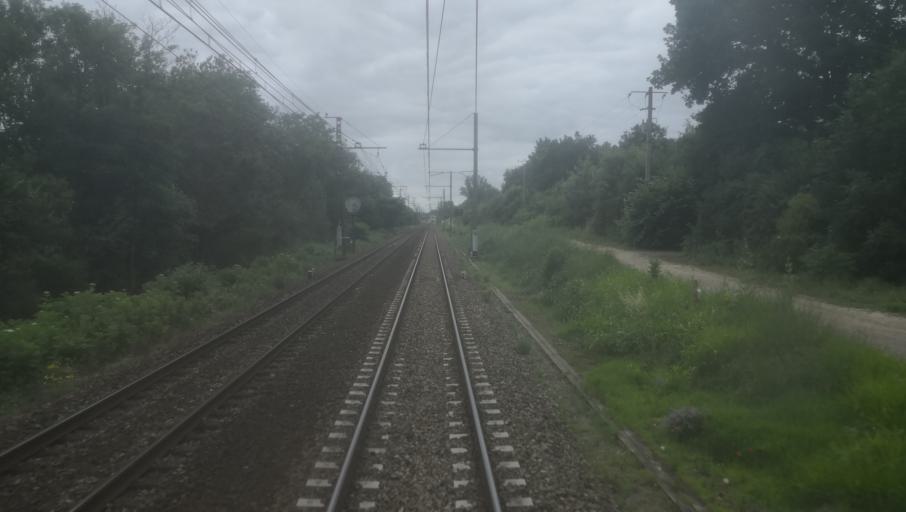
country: FR
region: Midi-Pyrenees
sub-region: Departement du Tarn-et-Garonne
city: Grisolles
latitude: 43.8591
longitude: 1.2809
